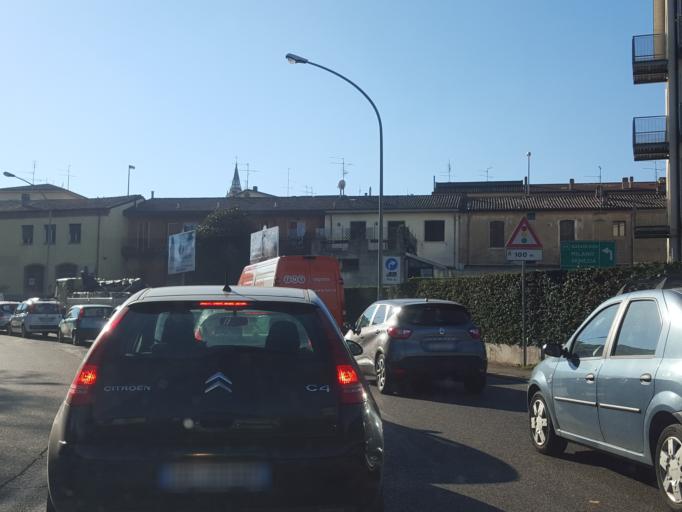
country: IT
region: Veneto
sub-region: Provincia di Verona
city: Verona
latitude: 45.4203
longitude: 10.9884
